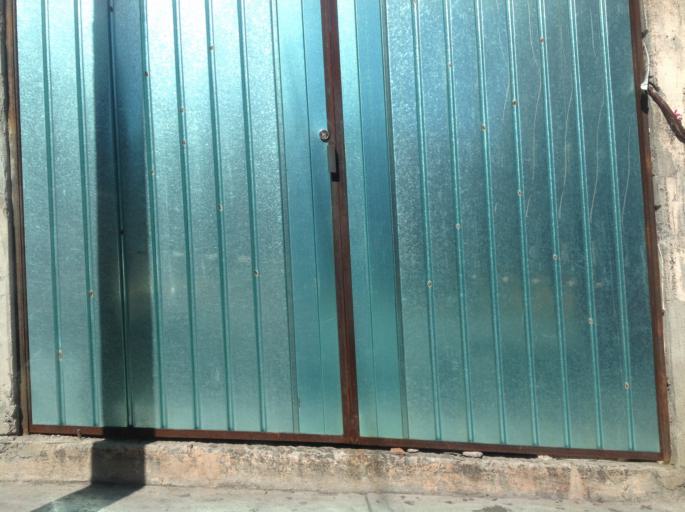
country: MX
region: Oaxaca
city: Ciudad de Huajuapam de Leon
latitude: 17.8082
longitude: -97.7744
